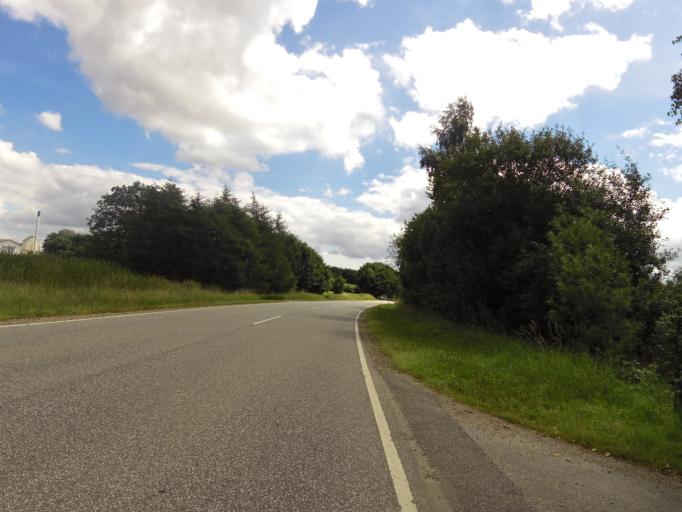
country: DK
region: South Denmark
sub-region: Haderslev Kommune
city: Haderslev
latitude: 55.2762
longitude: 9.4205
